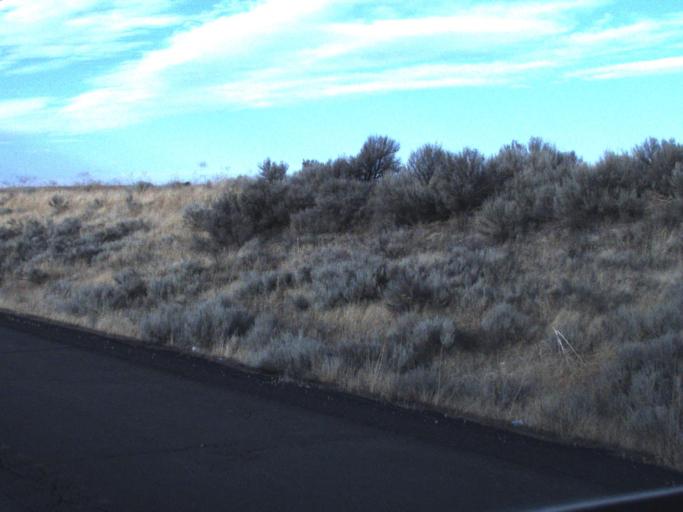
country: US
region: Washington
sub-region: Franklin County
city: Connell
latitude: 46.8087
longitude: -118.7197
